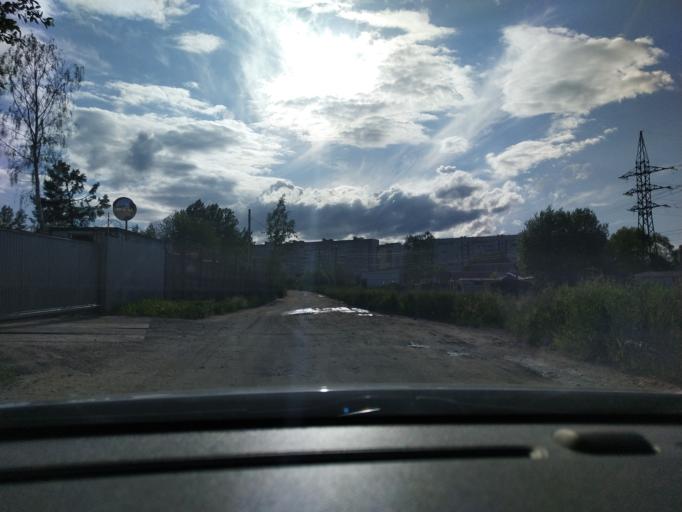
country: RU
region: St.-Petersburg
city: Gorelovo
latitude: 59.7848
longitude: 30.1561
